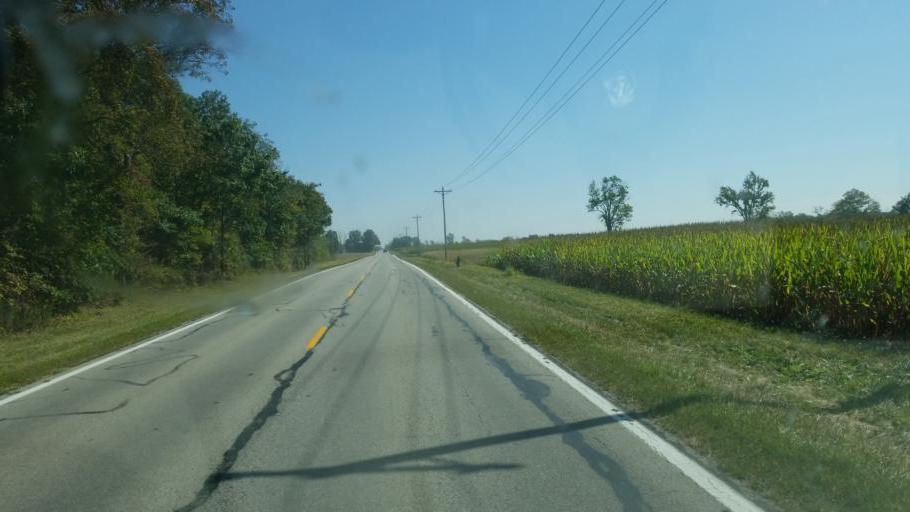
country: US
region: Ohio
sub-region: Hardin County
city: Forest
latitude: 40.6435
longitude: -83.3787
